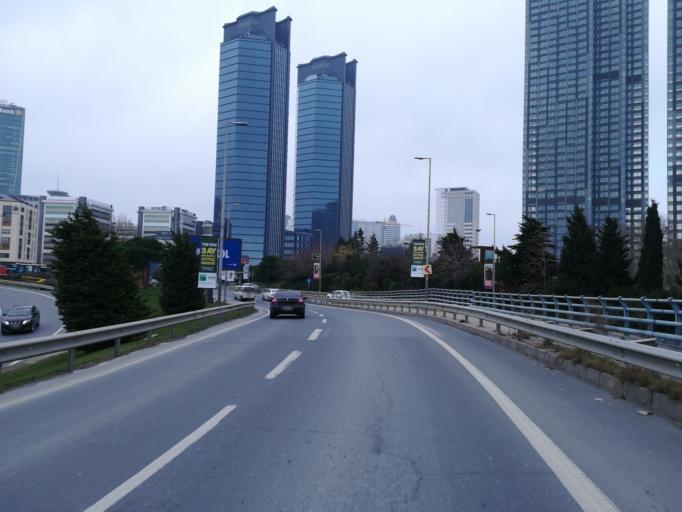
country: TR
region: Istanbul
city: Sisli
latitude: 41.0664
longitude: 29.0148
